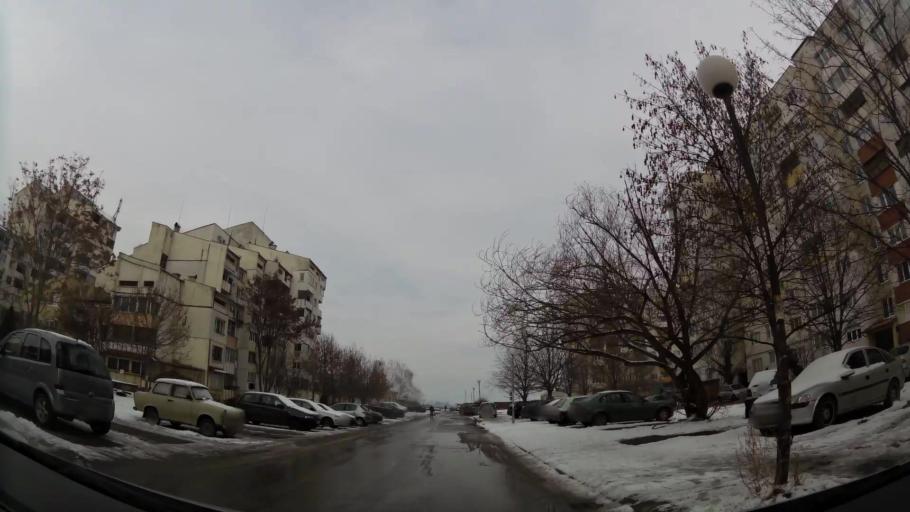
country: BG
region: Sofia-Capital
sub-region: Stolichna Obshtina
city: Sofia
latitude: 42.7147
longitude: 23.3760
